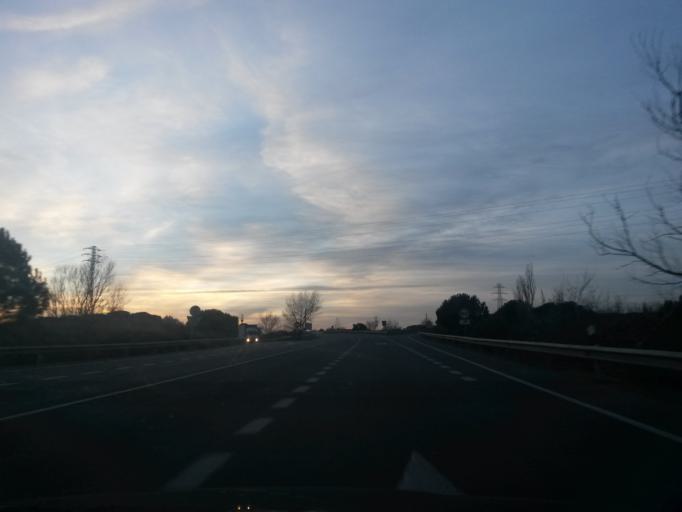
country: ES
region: Catalonia
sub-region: Provincia de Girona
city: Fornells de la Selva
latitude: 41.9418
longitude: 2.8210
